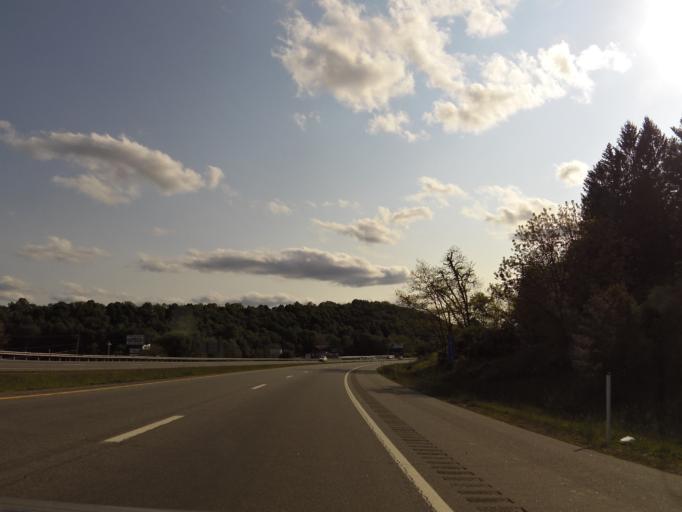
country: US
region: West Virginia
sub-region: Mercer County
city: Princeton
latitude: 37.3466
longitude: -81.1106
